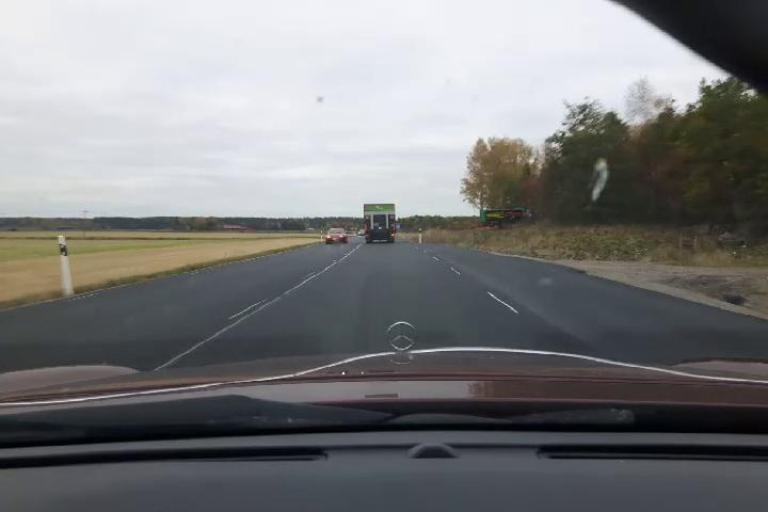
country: SE
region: Uppsala
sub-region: Enkopings Kommun
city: Enkoping
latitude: 59.6286
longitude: 17.0476
